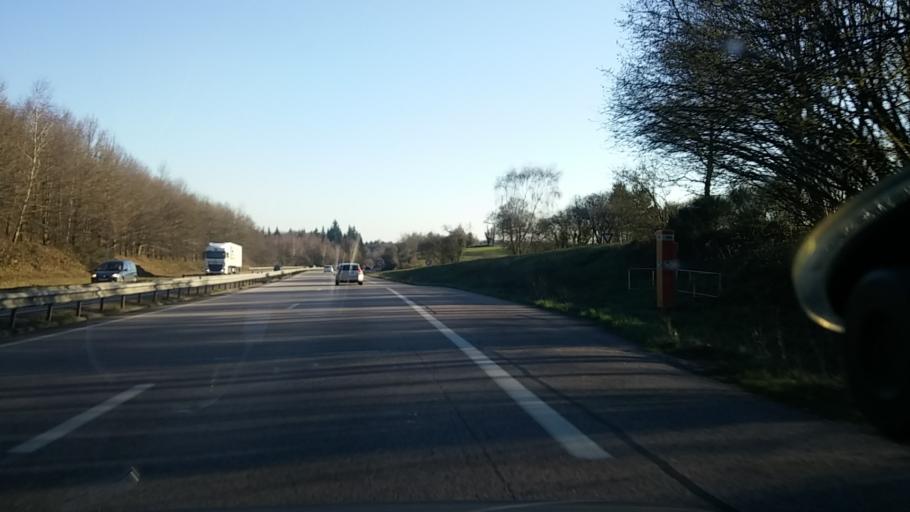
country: FR
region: Limousin
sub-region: Departement de la Haute-Vienne
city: Bonnac-la-Cote
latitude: 45.9382
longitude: 1.3046
